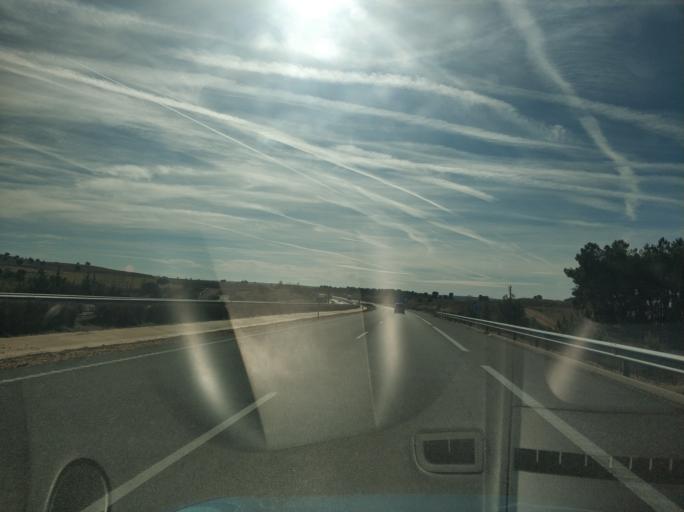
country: ES
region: Castille and Leon
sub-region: Provincia de Zamora
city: Cuelgamures
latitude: 41.2793
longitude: -5.7036
